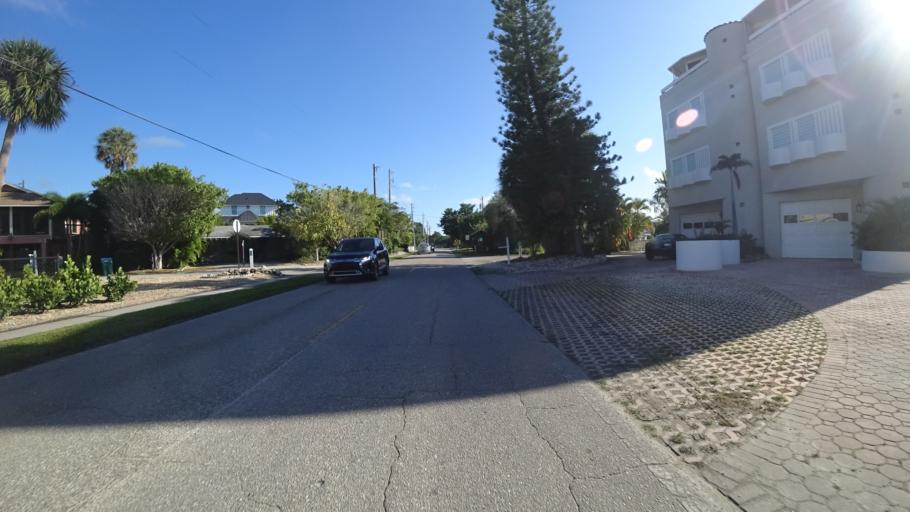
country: US
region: Florida
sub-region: Manatee County
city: Anna Maria
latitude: 27.5192
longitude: -82.7265
